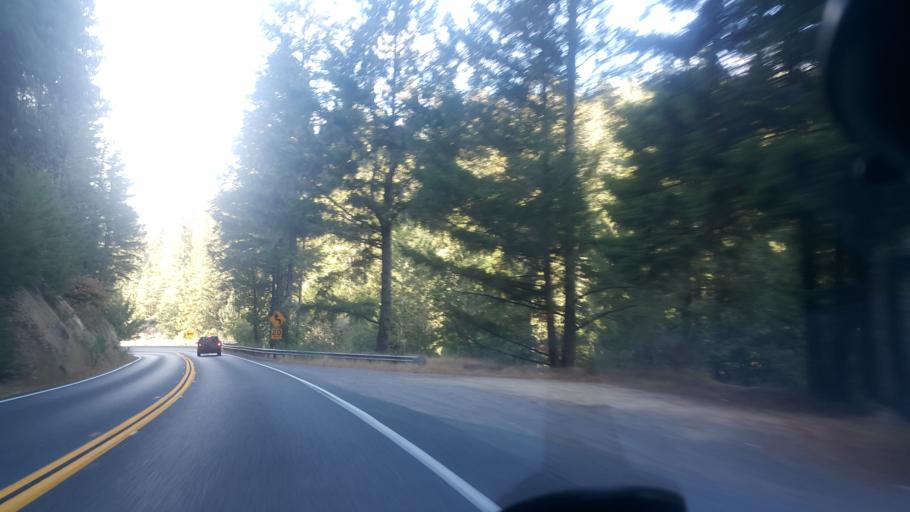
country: US
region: California
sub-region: Mendocino County
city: Brooktrails
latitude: 39.3550
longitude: -123.5101
